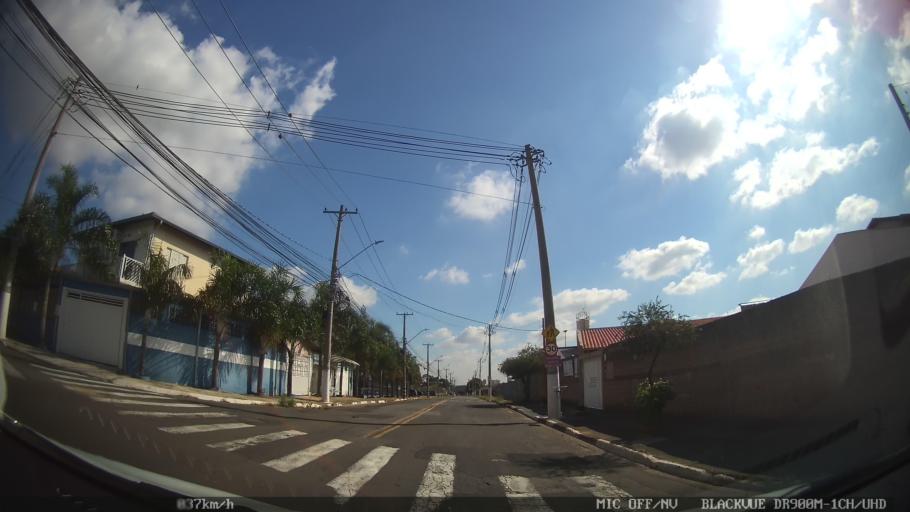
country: BR
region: Sao Paulo
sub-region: Hortolandia
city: Hortolandia
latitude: -22.8968
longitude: -47.1971
